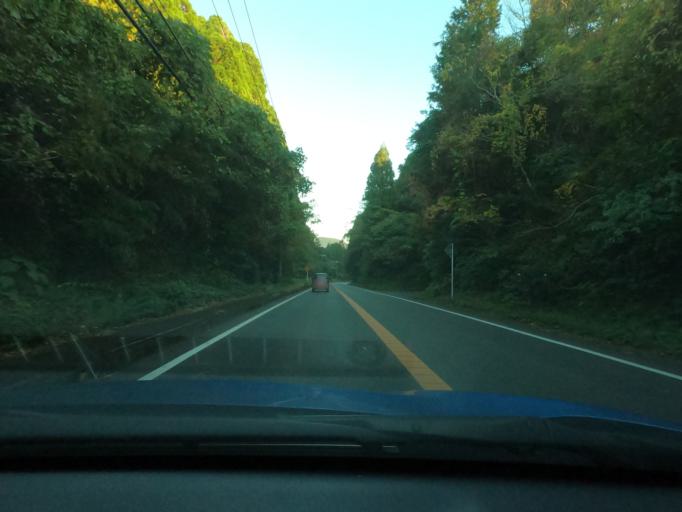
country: JP
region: Kagoshima
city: Satsumasendai
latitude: 31.8115
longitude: 130.3813
